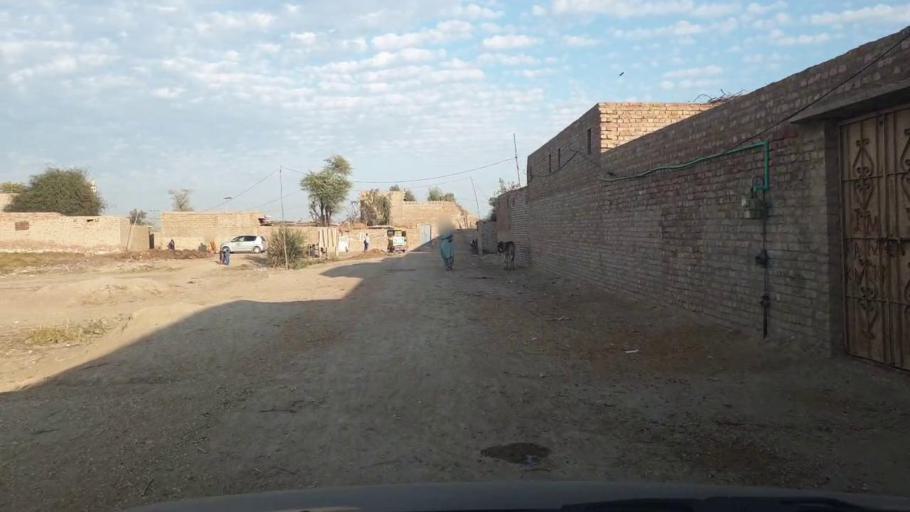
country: PK
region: Sindh
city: Sakrand
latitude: 26.0252
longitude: 68.3917
